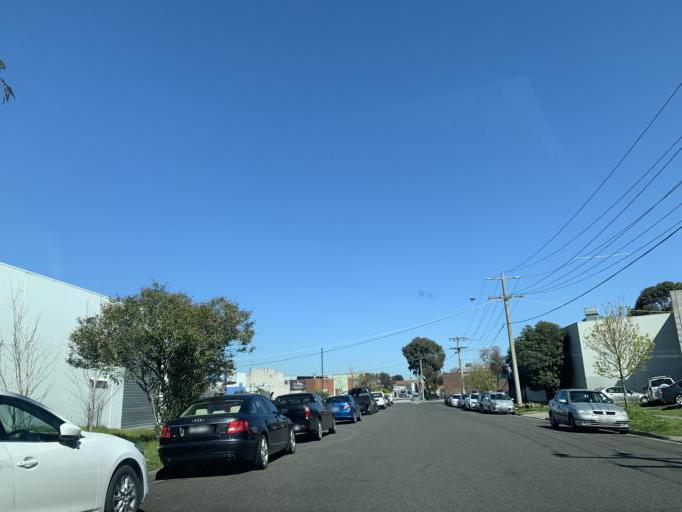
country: AU
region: Victoria
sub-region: Greater Dandenong
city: Dandenong
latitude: -37.9883
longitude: 145.2024
